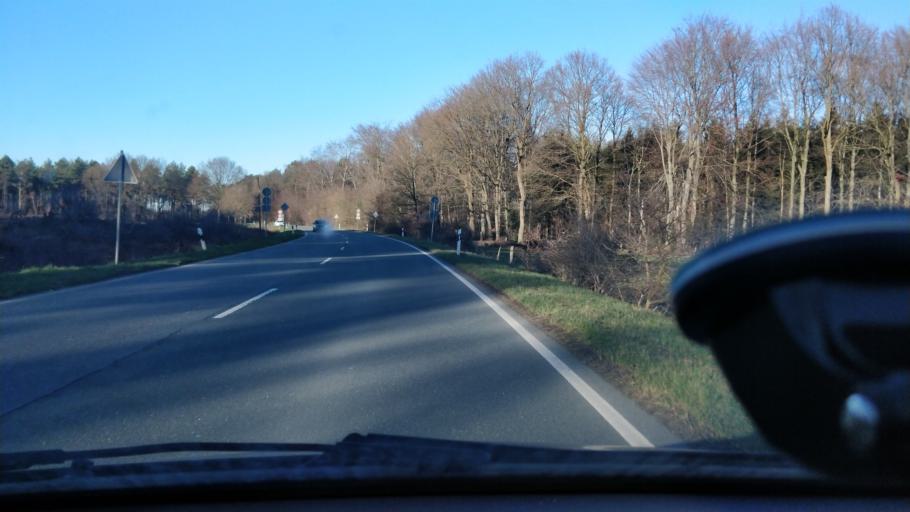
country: DE
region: North Rhine-Westphalia
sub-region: Regierungsbezirk Munster
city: Bottrop
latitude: 51.5780
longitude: 6.8839
